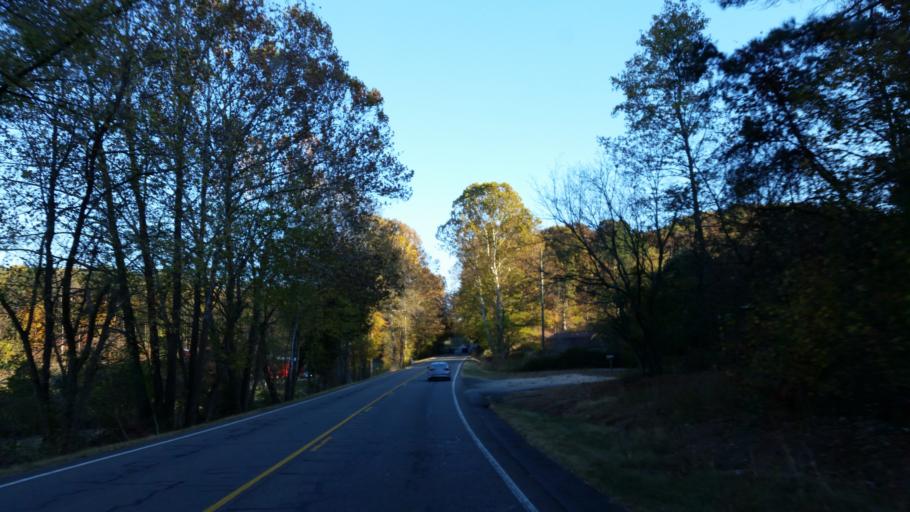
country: US
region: Georgia
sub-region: Gilmer County
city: Ellijay
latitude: 34.6177
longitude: -84.3672
